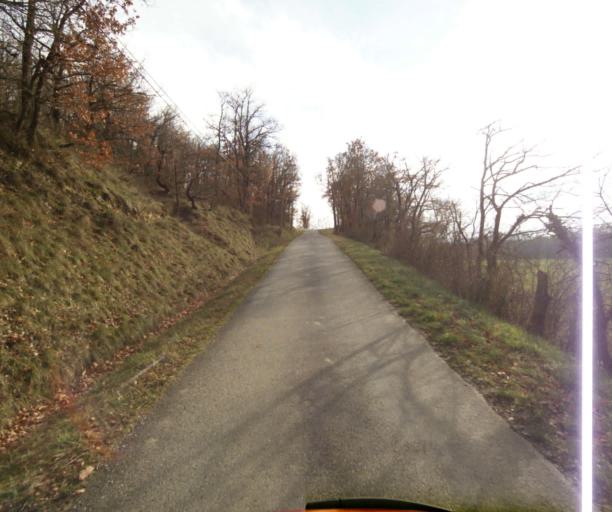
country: FR
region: Languedoc-Roussillon
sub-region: Departement de l'Aude
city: Belpech
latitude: 43.1692
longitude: 1.7378
